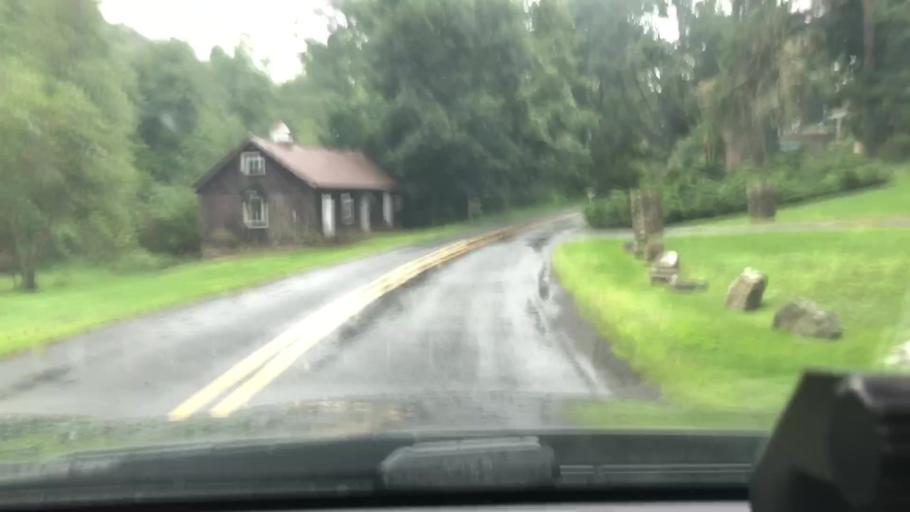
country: US
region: Pennsylvania
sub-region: Lehigh County
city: Macungie
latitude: 40.4693
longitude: -75.5487
